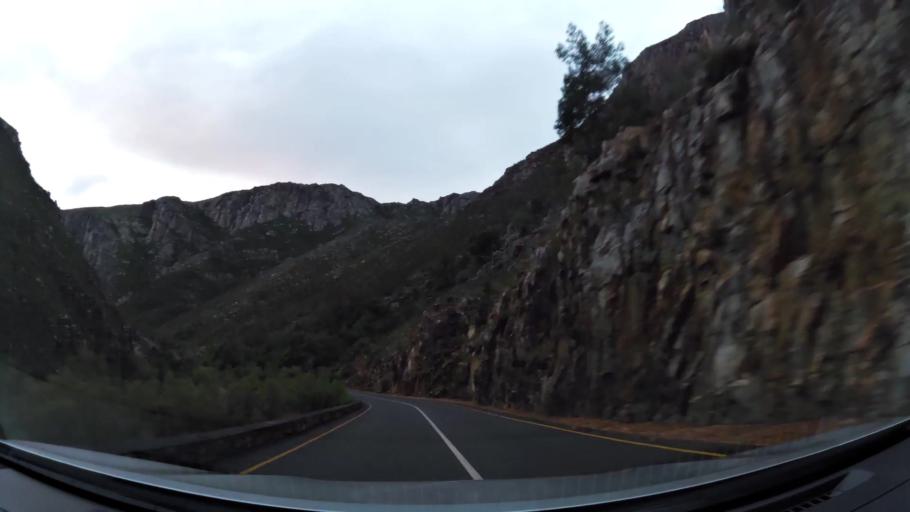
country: ZA
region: Western Cape
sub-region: Overberg District Municipality
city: Swellendam
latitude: -33.9599
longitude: 20.7072
